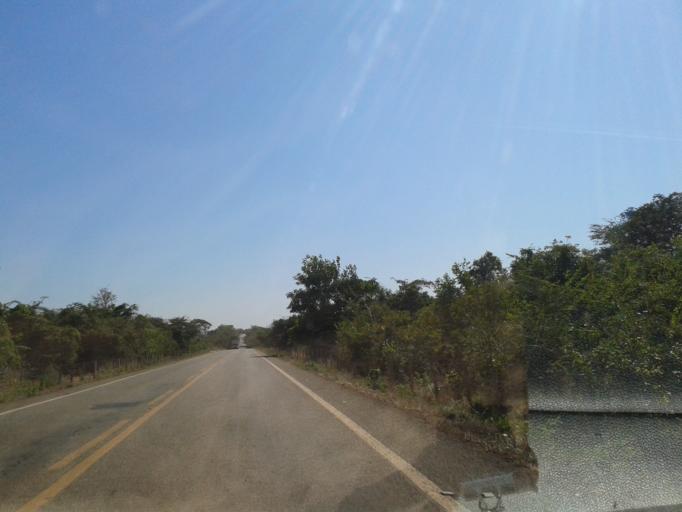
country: BR
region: Goias
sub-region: Crixas
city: Crixas
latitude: -14.0424
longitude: -50.3292
